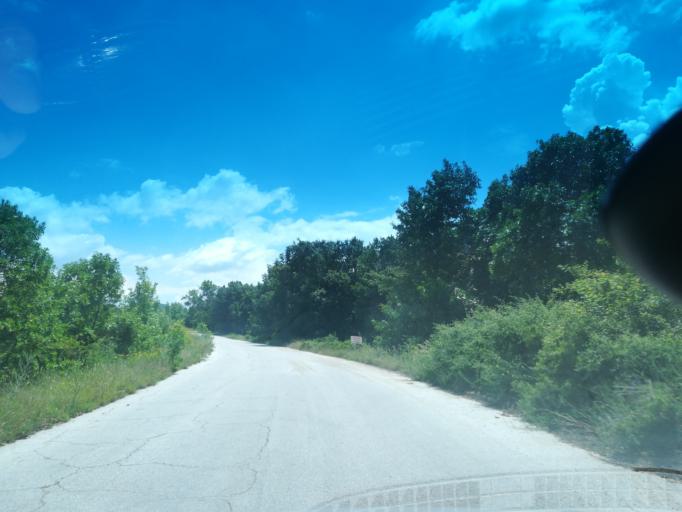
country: BG
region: Khaskovo
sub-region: Obshtina Mineralni Bani
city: Mineralni Bani
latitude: 41.9875
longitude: 25.2414
